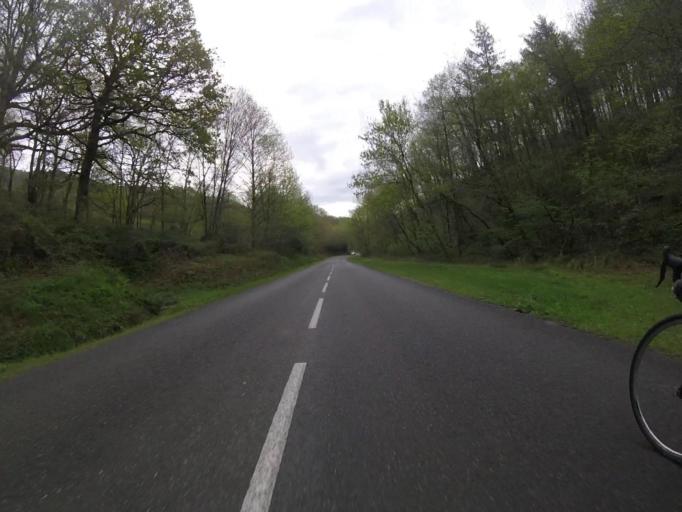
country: FR
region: Aquitaine
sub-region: Departement des Pyrenees-Atlantiques
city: Sare
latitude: 43.2847
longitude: -1.6240
